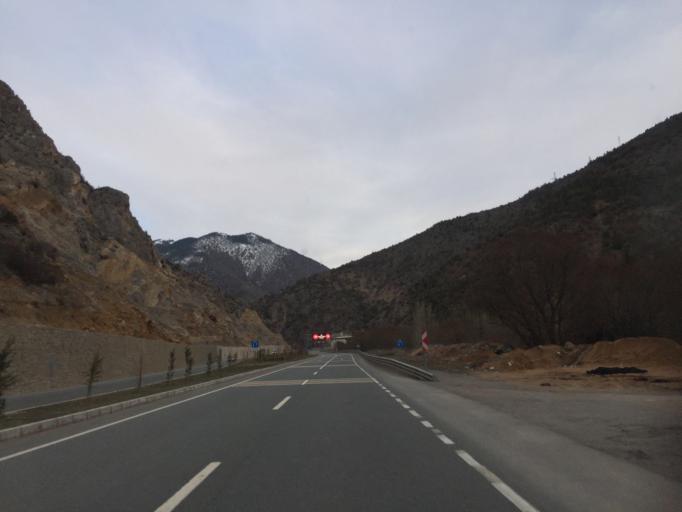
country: TR
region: Gumushane
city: Gumushkhane
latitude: 40.5208
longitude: 39.4048
